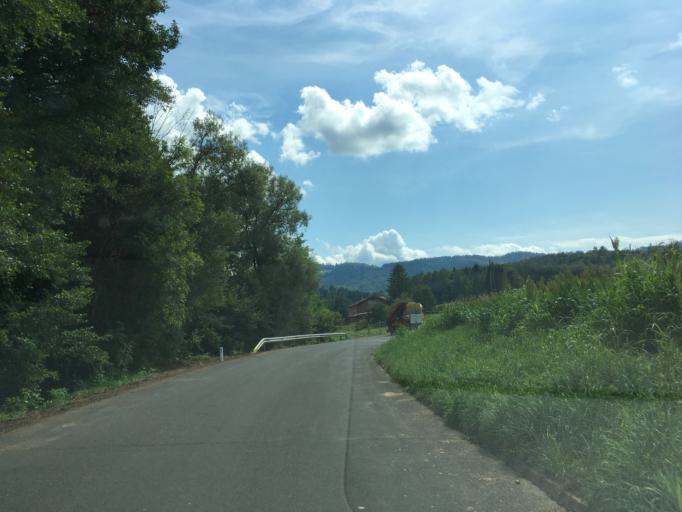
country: AT
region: Styria
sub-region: Politischer Bezirk Leibnitz
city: Oberhaag
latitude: 46.6830
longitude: 15.3524
